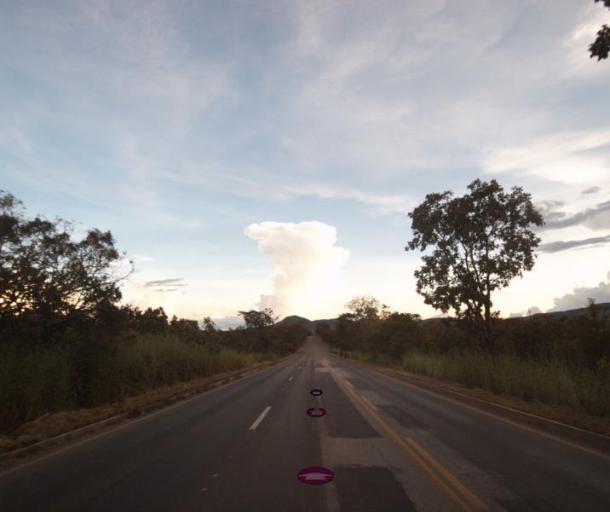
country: BR
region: Goias
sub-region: Uruacu
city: Uruacu
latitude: -14.3474
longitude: -49.1576
